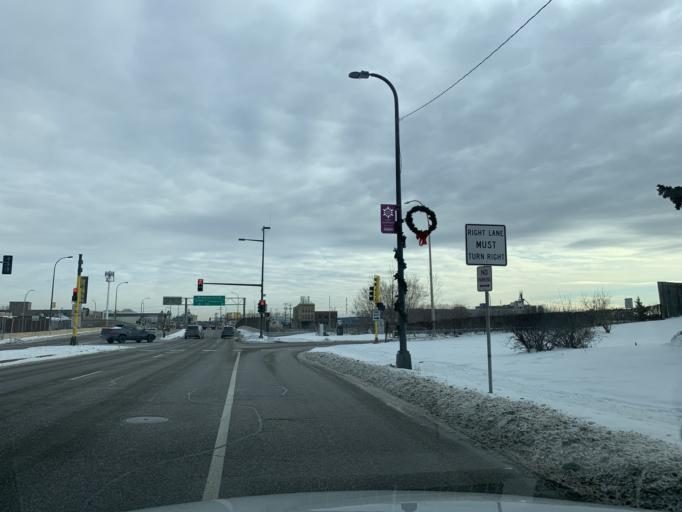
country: US
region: Minnesota
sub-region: Hennepin County
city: Minneapolis
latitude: 44.9991
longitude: -93.2846
